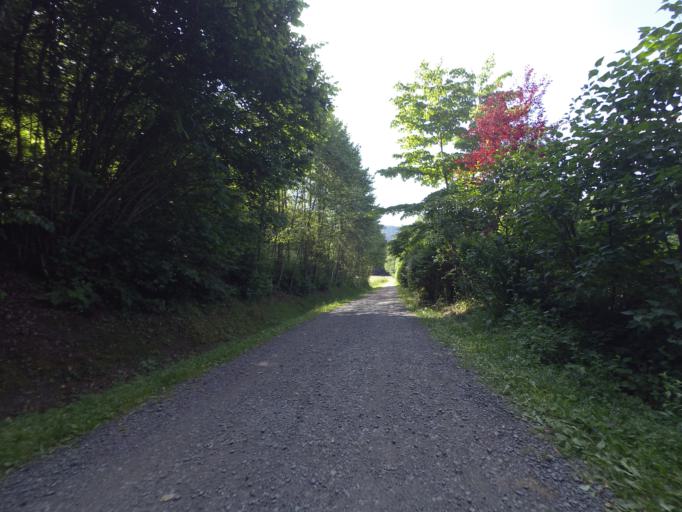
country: AT
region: Carinthia
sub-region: Politischer Bezirk Spittal an der Drau
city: Millstatt
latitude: 46.7729
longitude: 13.6044
